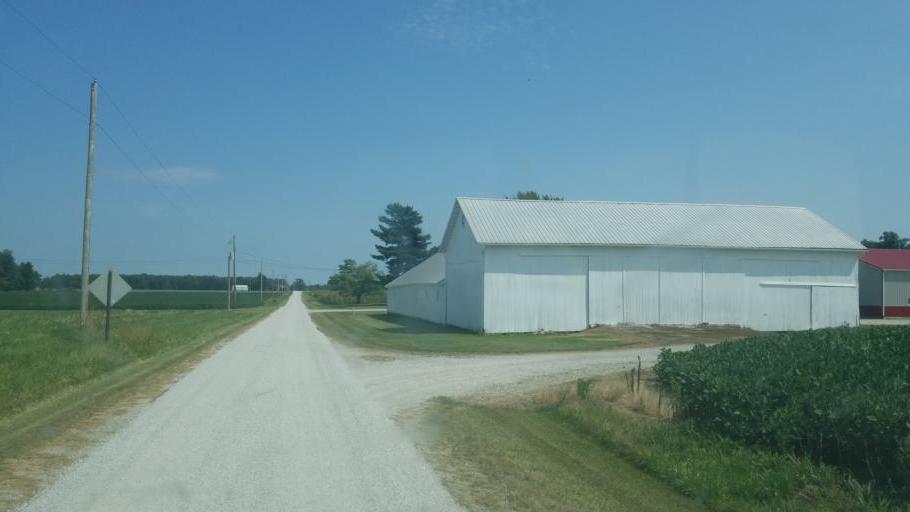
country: US
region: Ohio
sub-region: Crawford County
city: Bucyrus
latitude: 40.9357
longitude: -82.9460
